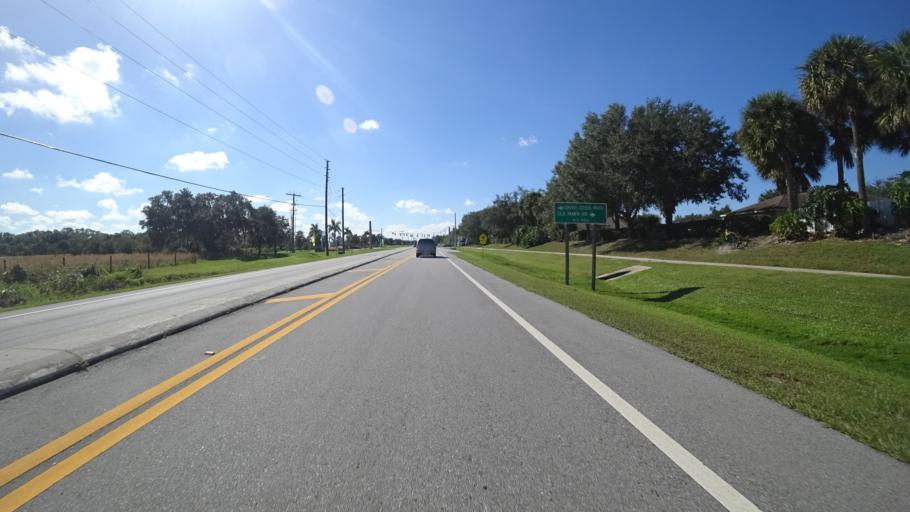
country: US
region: Florida
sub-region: Manatee County
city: Ellenton
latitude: 27.5498
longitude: -82.4255
